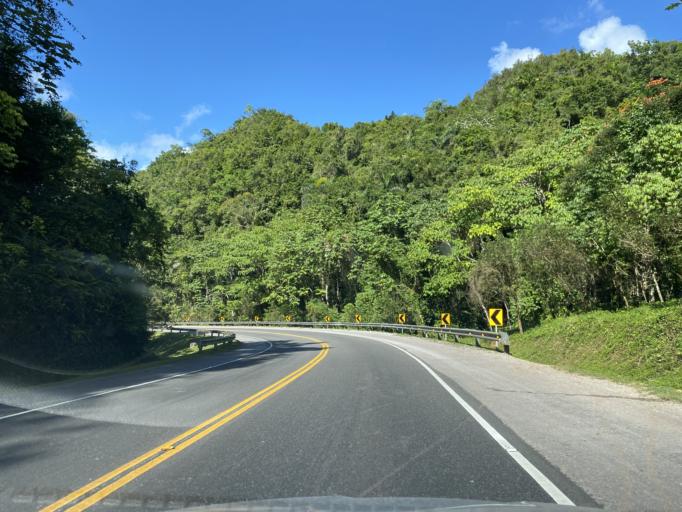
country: DO
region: Monte Plata
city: Majagual
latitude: 19.0607
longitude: -69.8273
